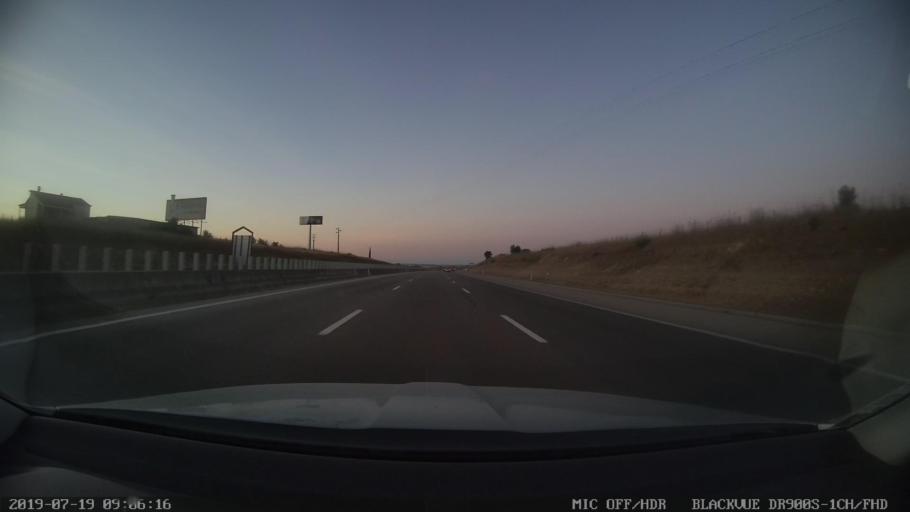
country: PT
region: Santarem
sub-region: Santarem
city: Santarem
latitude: 39.3084
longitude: -8.6754
